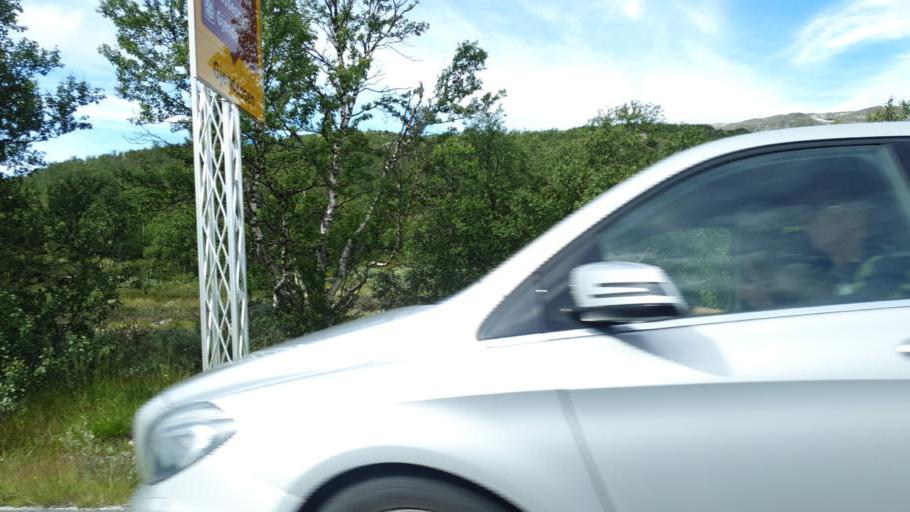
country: NO
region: Oppland
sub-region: Oystre Slidre
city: Heggenes
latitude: 61.4930
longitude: 8.8429
